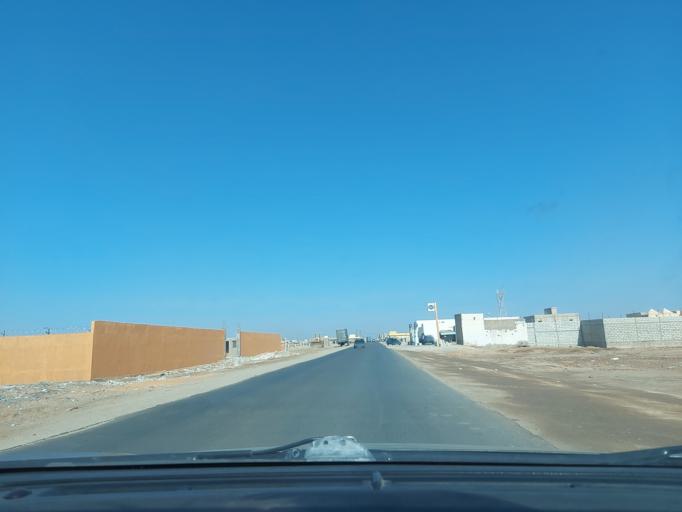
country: MR
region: Nouakchott
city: Nouakchott
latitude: 18.0113
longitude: -15.9845
